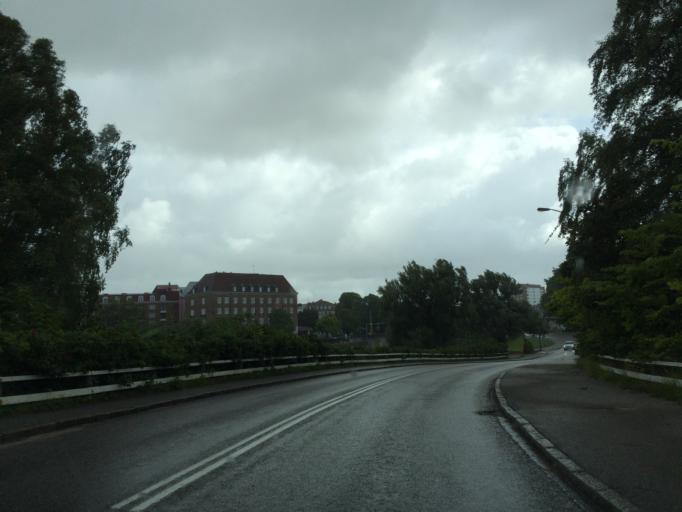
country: SE
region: Vaestra Goetaland
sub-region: Trollhattan
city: Trollhattan
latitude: 58.2859
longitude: 12.2825
